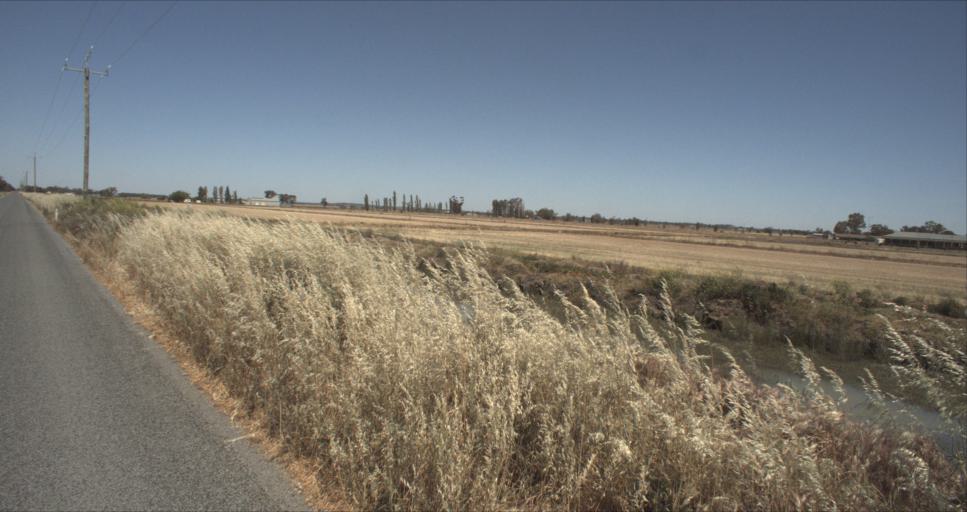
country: AU
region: New South Wales
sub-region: Leeton
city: Leeton
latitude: -34.5087
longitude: 146.4250
